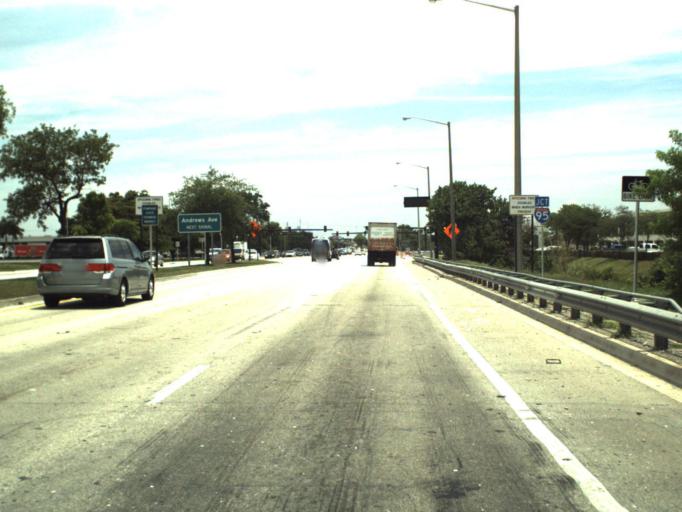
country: US
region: Florida
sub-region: Broward County
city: Pompano Beach
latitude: 26.2313
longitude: -80.1438
